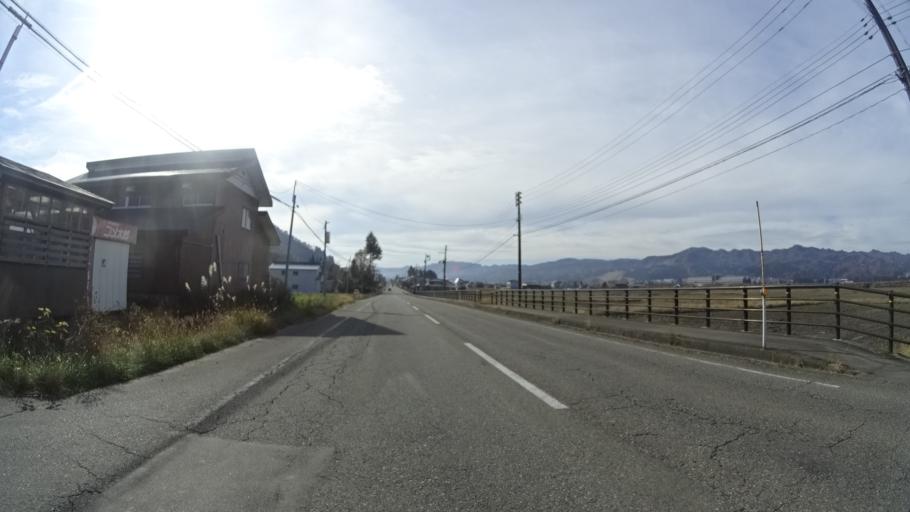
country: JP
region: Niigata
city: Muikamachi
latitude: 37.1260
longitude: 138.9326
